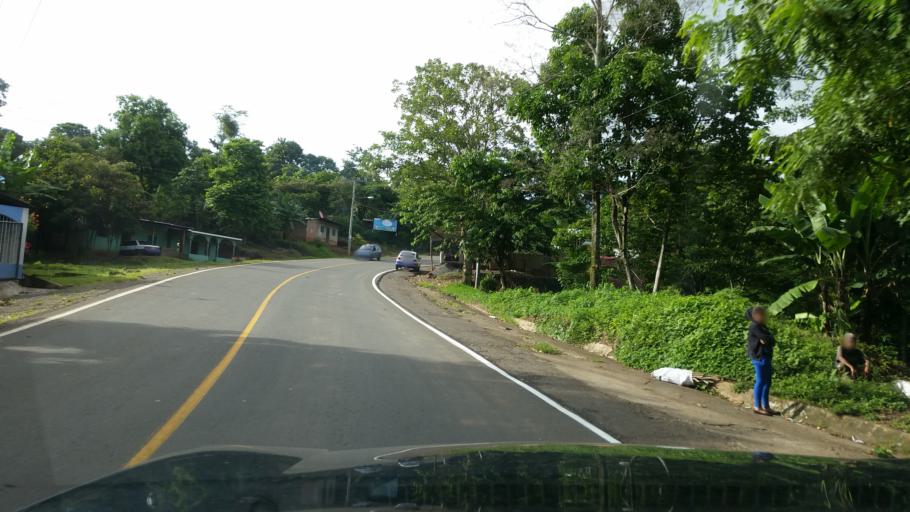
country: NI
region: Matagalpa
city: San Ramon
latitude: 13.1330
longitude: -85.7372
